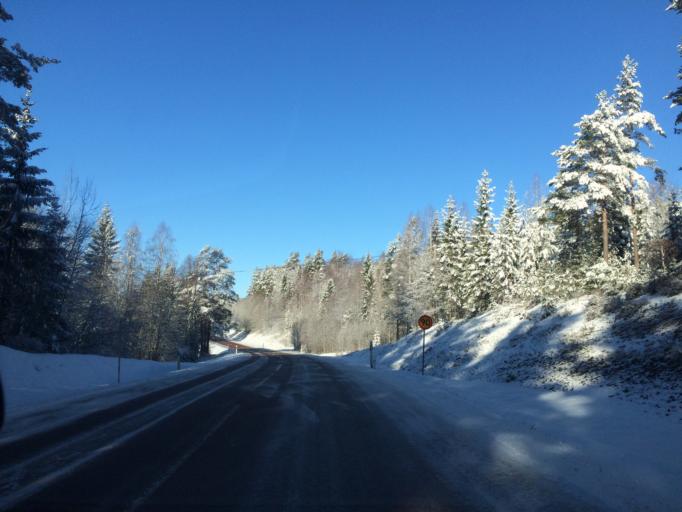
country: SE
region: Dalarna
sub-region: Vansbro Kommun
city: Vansbro
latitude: 60.8552
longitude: 14.2308
